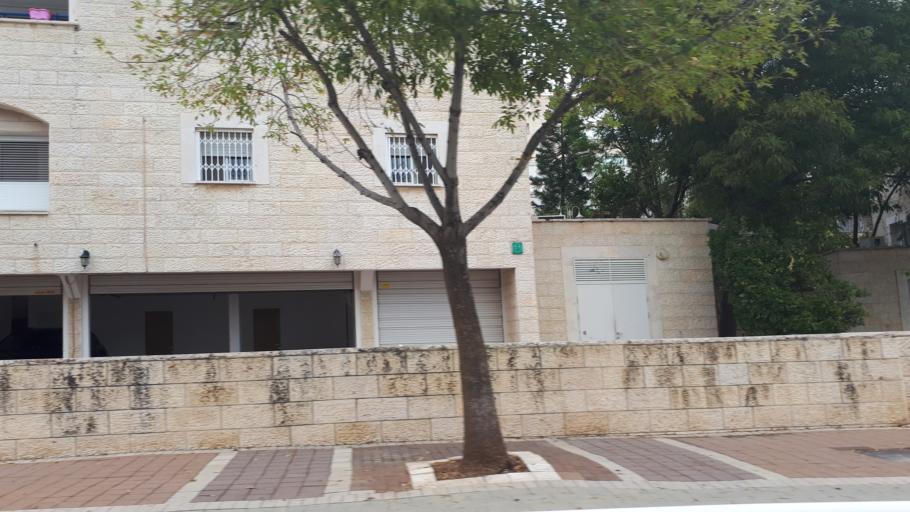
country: IL
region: Central District
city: Modiin
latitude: 31.9032
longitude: 35.0096
